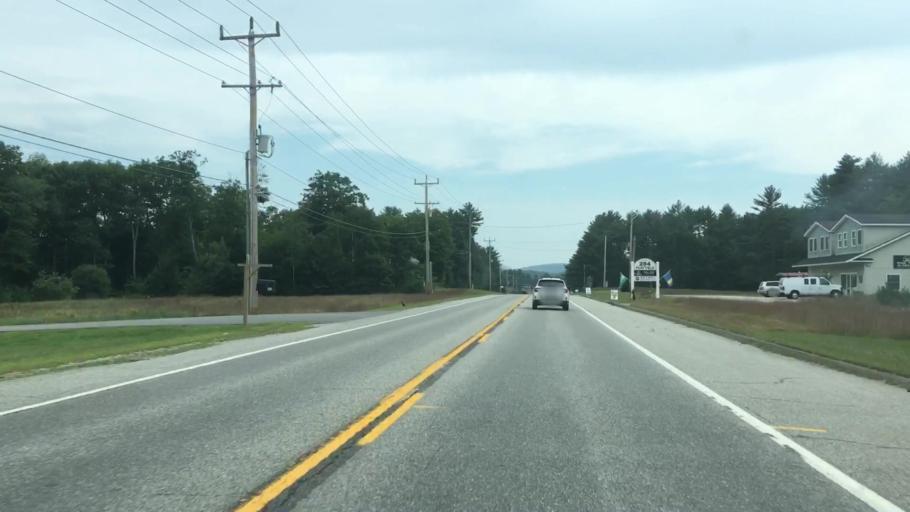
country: US
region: Maine
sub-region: Oxford County
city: Bethel
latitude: 44.4305
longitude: -70.8002
